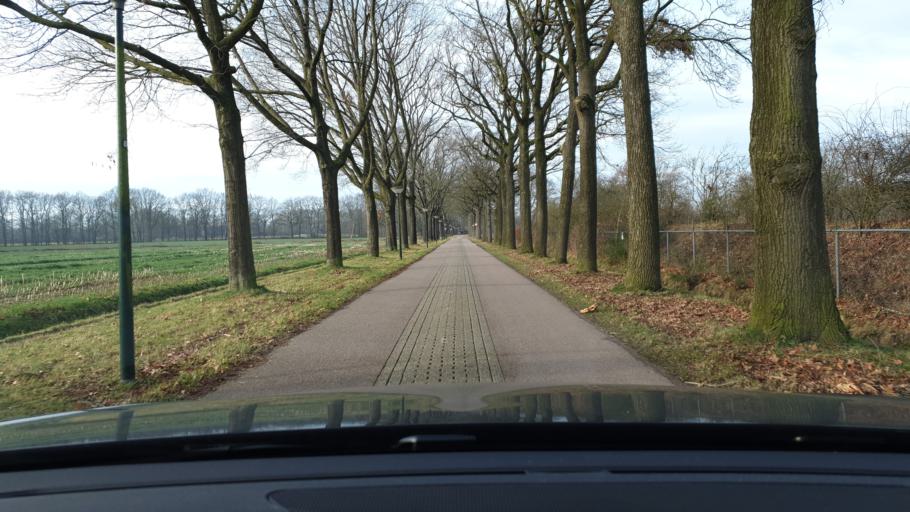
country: NL
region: North Brabant
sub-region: Gemeente Eindhoven
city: Muschberg en Geestenberg
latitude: 51.4215
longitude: 5.5319
